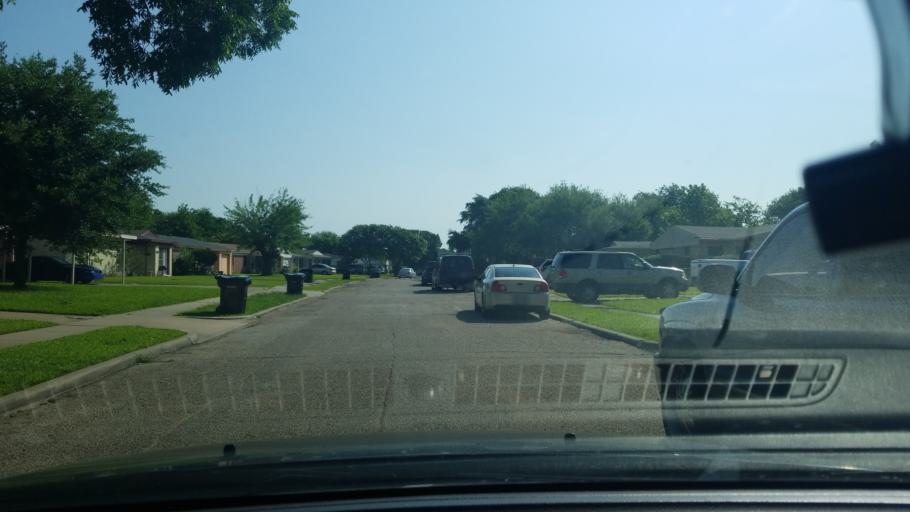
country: US
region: Texas
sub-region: Dallas County
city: Mesquite
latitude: 32.8285
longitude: -96.6439
